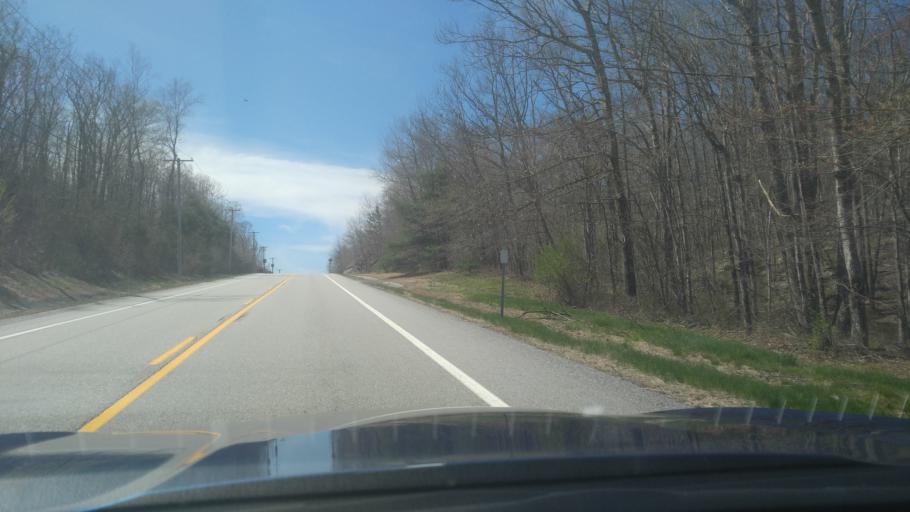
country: US
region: Rhode Island
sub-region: Washington County
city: Hope Valley
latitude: 41.5742
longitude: -71.7330
